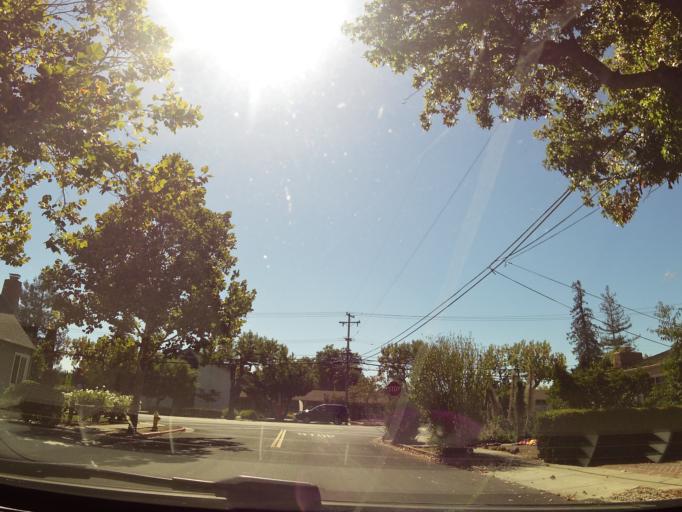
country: US
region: California
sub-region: Santa Clara County
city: Campbell
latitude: 37.2874
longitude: -121.9562
